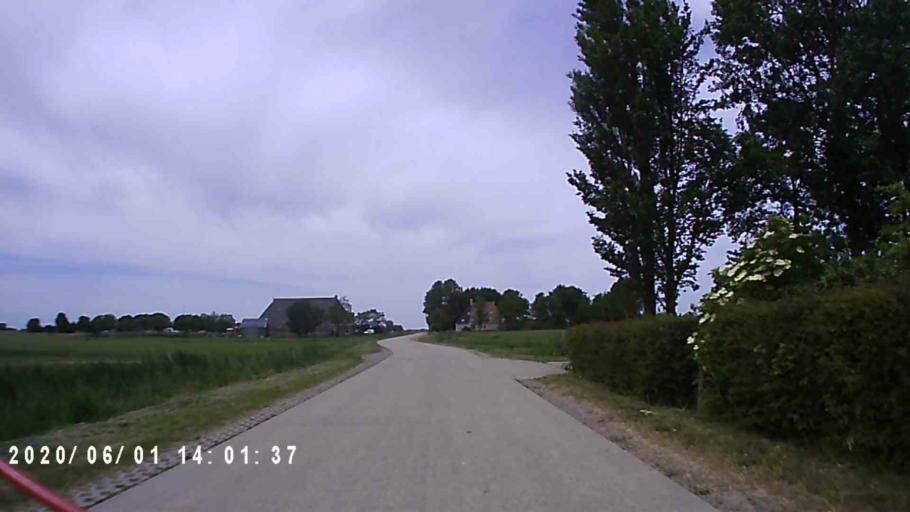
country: NL
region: Friesland
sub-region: Gemeente Littenseradiel
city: Makkum
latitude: 53.1084
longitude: 5.6433
